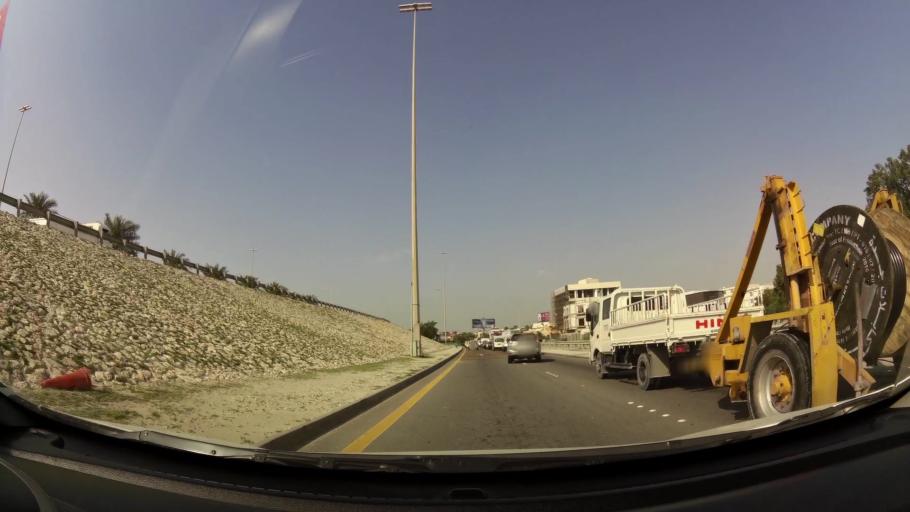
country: BH
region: Manama
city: Jidd Hafs
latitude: 26.2161
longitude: 50.5211
